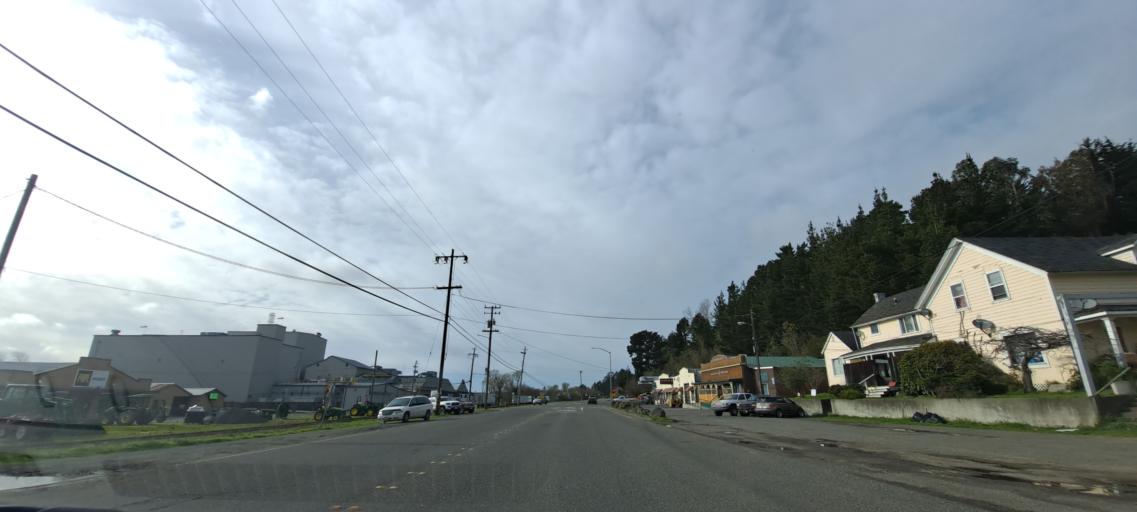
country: US
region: California
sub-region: Humboldt County
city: Fortuna
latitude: 40.6159
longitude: -124.2007
